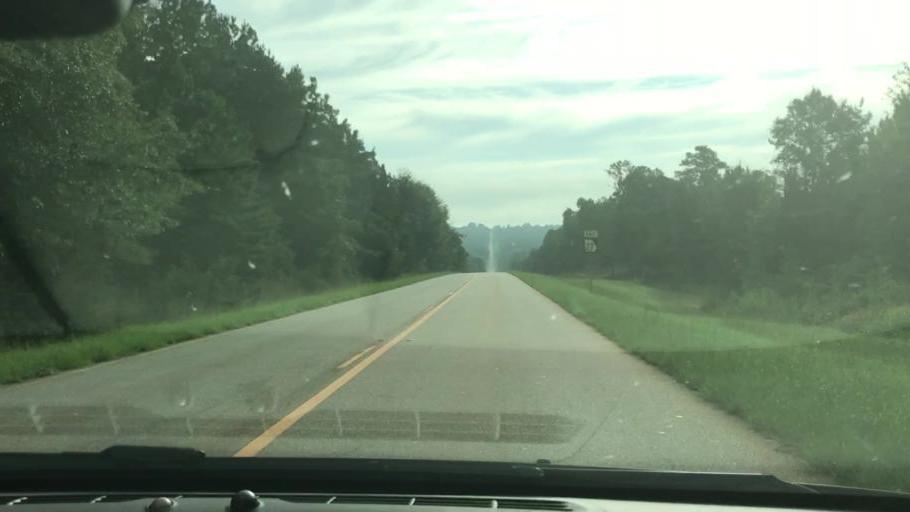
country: US
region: Georgia
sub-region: Quitman County
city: Georgetown
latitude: 31.9753
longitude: -84.9729
